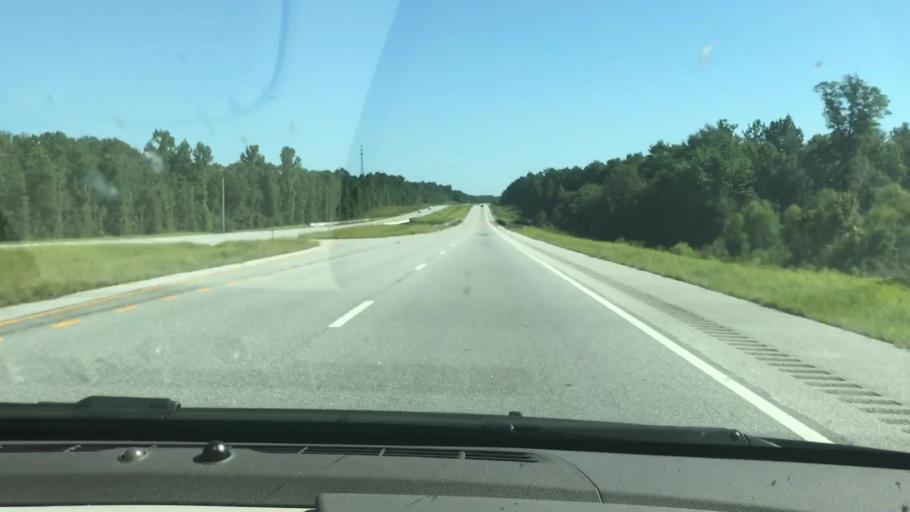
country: US
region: Alabama
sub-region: Russell County
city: Ladonia
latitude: 32.3792
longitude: -85.0852
